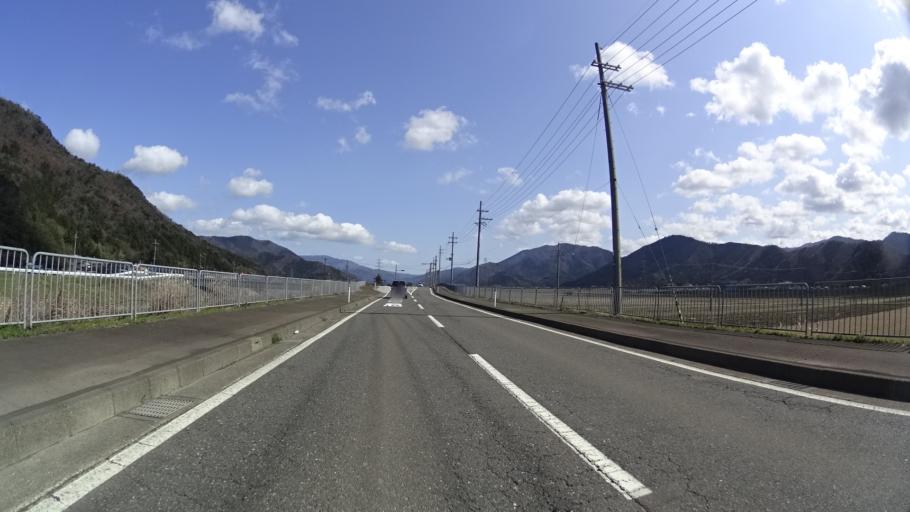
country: JP
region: Fukui
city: Obama
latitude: 35.4846
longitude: 135.8008
